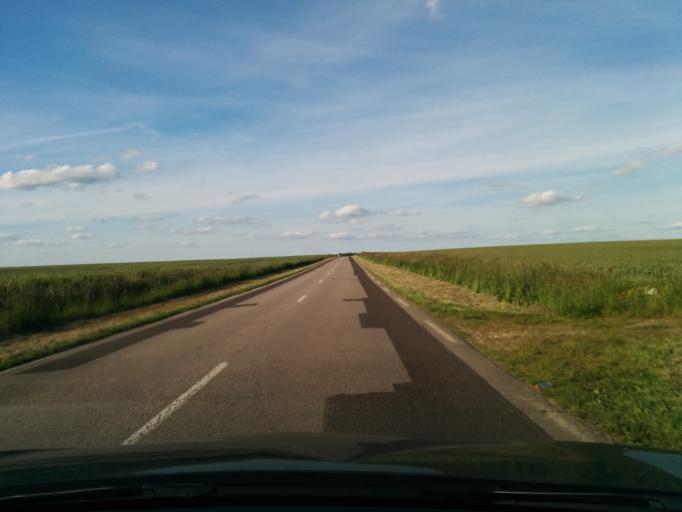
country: FR
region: Haute-Normandie
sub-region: Departement de l'Eure
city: Les Andelys
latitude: 49.2922
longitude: 1.4178
